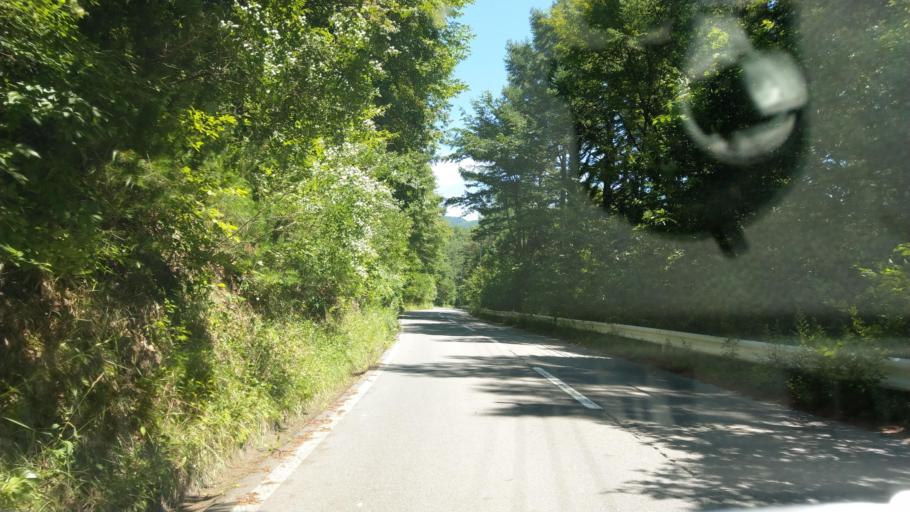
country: JP
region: Nagano
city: Komoro
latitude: 36.3658
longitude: 138.4587
